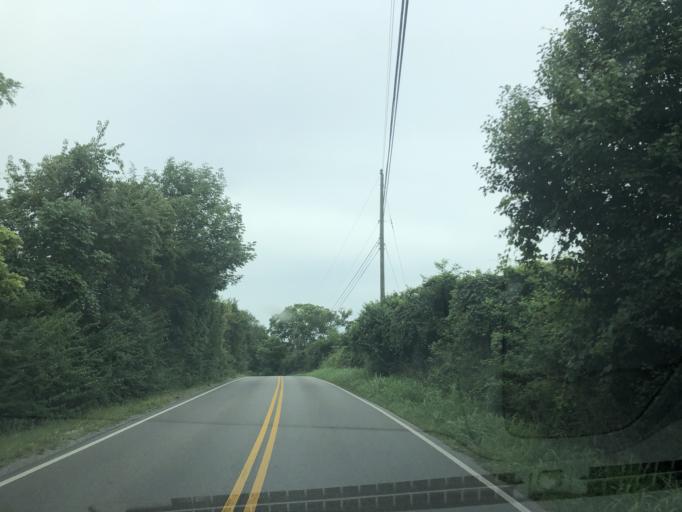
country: US
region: Tennessee
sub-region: Williamson County
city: Nolensville
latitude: 36.0347
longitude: -86.6874
